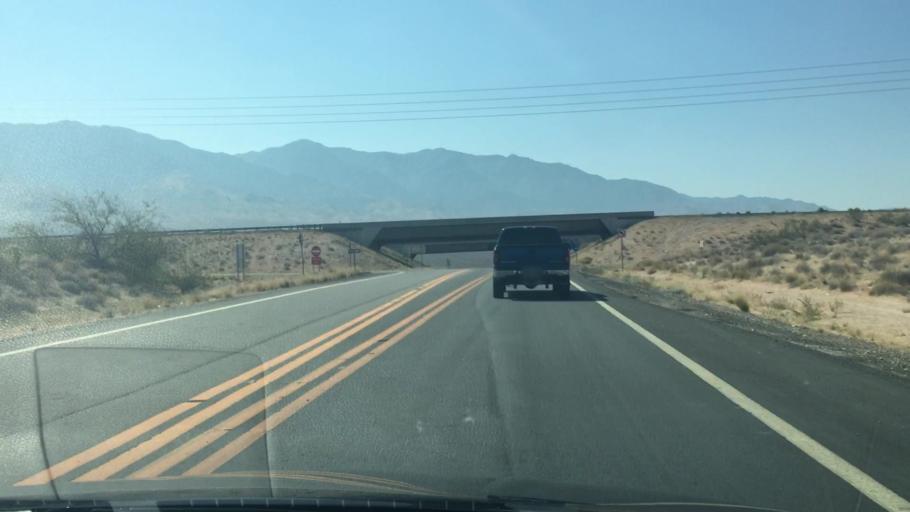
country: US
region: Arizona
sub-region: Mohave County
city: Beaver Dam
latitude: 36.8933
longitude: -113.9303
